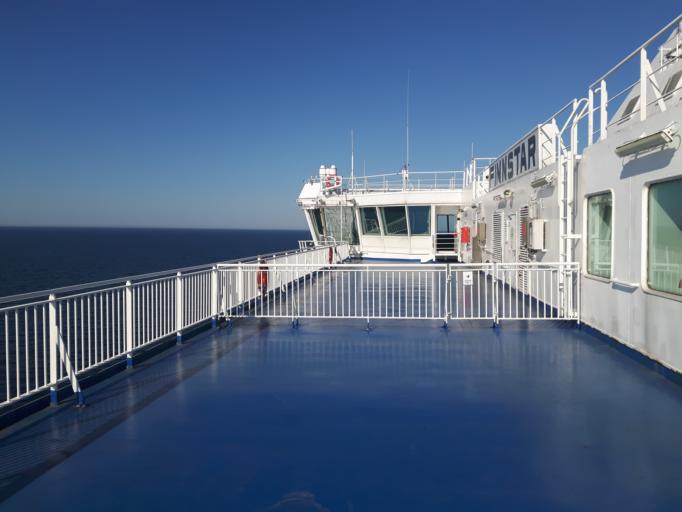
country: SE
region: Gotland
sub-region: Gotland
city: Hemse
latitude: 56.5951
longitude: 17.9536
